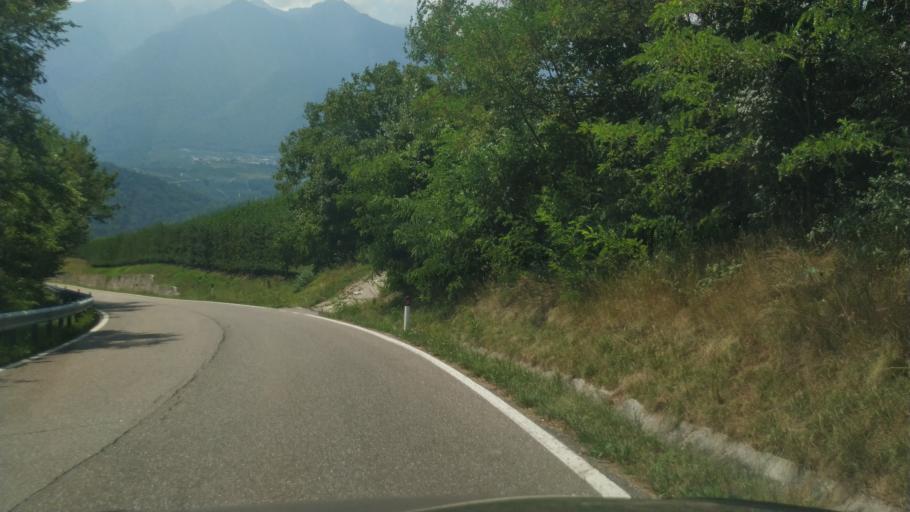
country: IT
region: Trentino-Alto Adige
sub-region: Provincia di Trento
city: Vigo di Ton
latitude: 46.2518
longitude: 11.0684
